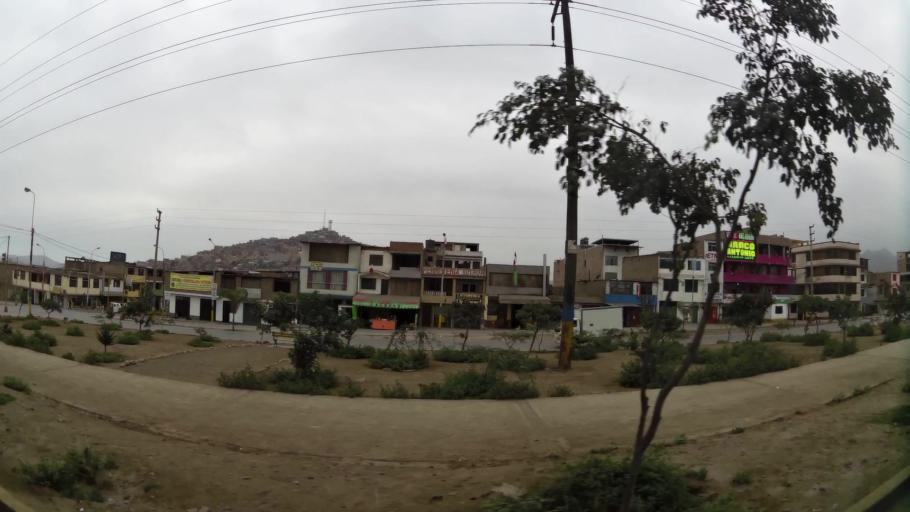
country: PE
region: Lima
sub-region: Lima
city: Surco
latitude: -12.1916
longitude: -76.9459
